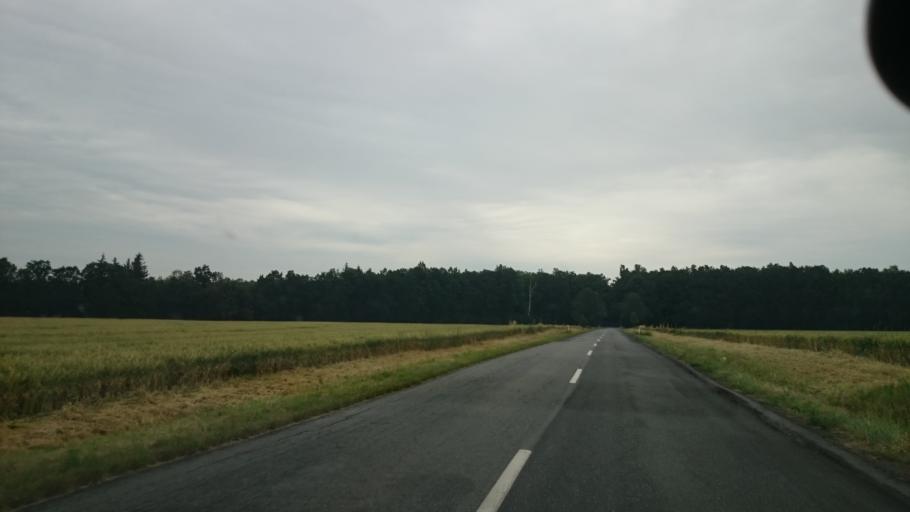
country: PL
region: Lower Silesian Voivodeship
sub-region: Powiat strzelinski
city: Przeworno
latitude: 50.6509
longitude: 17.2321
